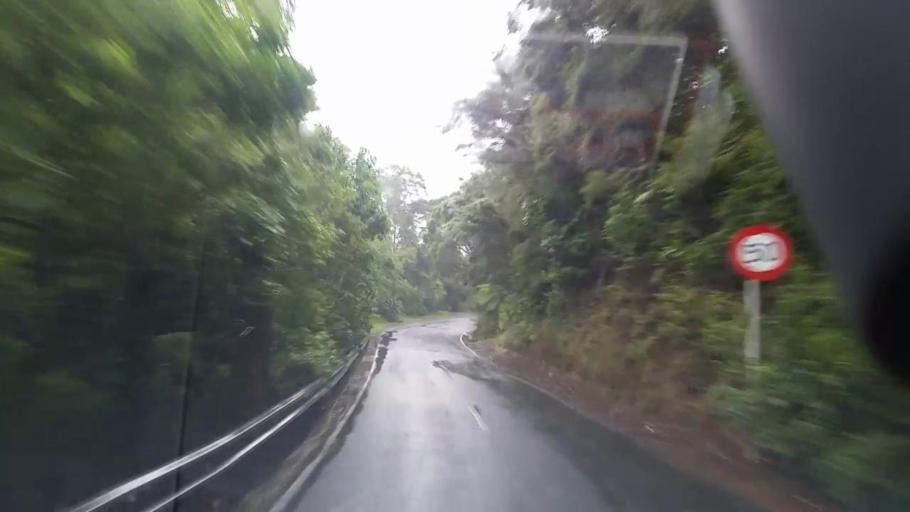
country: NZ
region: Auckland
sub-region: Auckland
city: Waitakere
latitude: -36.9049
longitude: 174.5709
